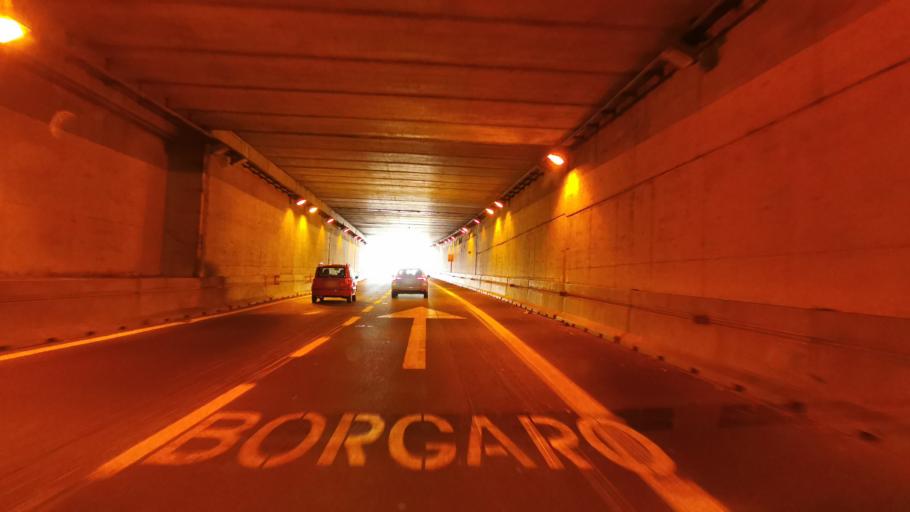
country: IT
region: Piedmont
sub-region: Provincia di Torino
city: Borgaro Torinese
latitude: 45.1446
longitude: 7.6508
